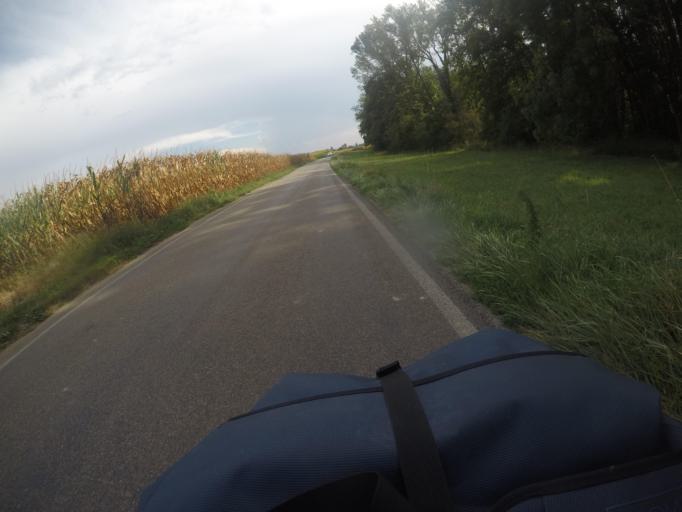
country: DE
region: Baden-Wuerttemberg
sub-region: Freiburg Region
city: Efringen-Kirchen
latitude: 47.6386
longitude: 7.5704
